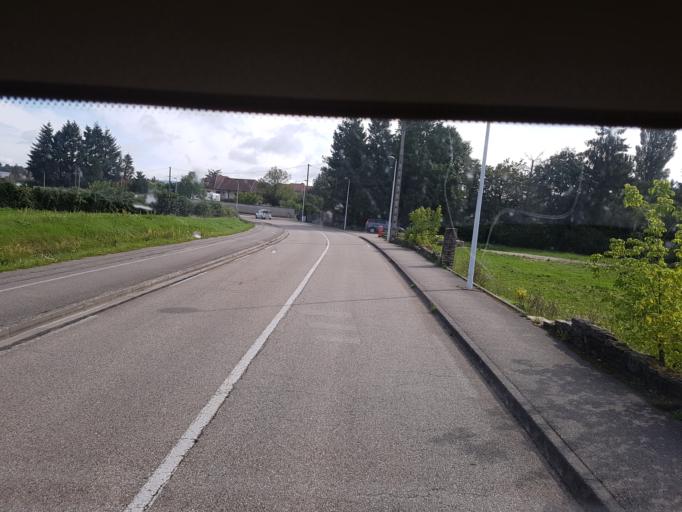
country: FR
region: Rhone-Alpes
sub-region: Departement de l'Ain
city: Bourg-en-Bresse
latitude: 46.1940
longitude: 5.2596
